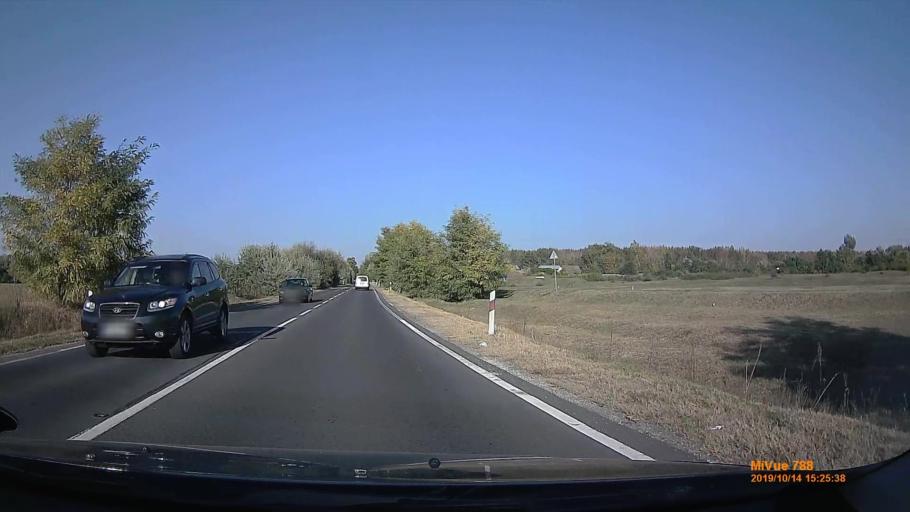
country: HU
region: Pest
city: Vecses
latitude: 47.4110
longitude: 19.3115
